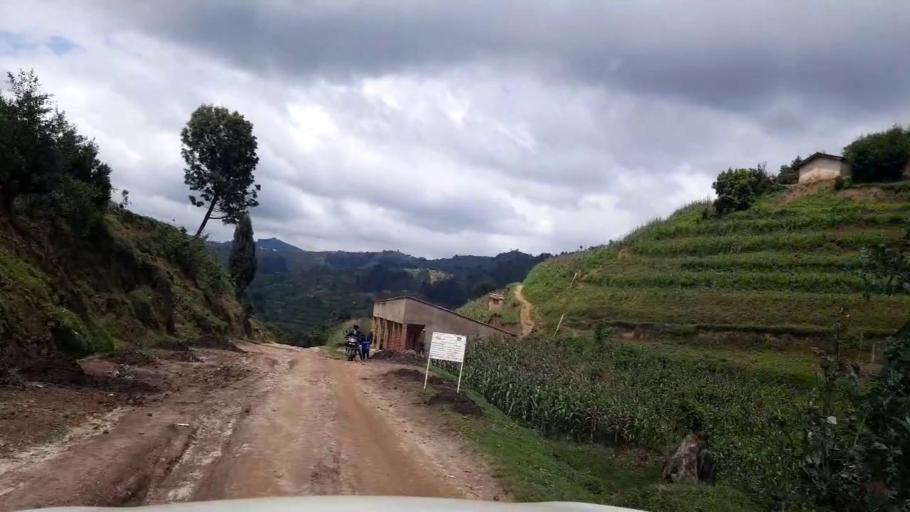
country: RW
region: Western Province
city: Kibuye
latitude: -1.9218
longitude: 29.4560
